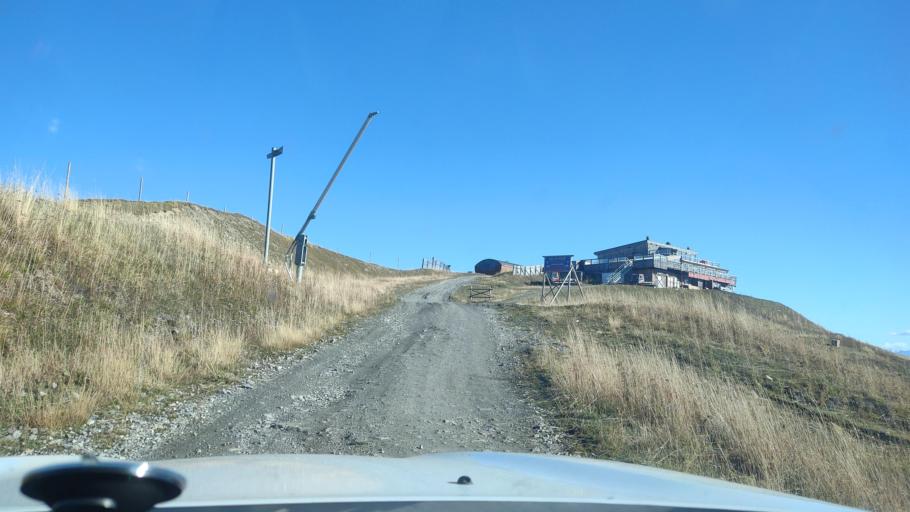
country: FR
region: Rhone-Alpes
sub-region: Departement de la Savoie
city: Saint-Etienne-de-Cuines
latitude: 45.2550
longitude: 6.2296
